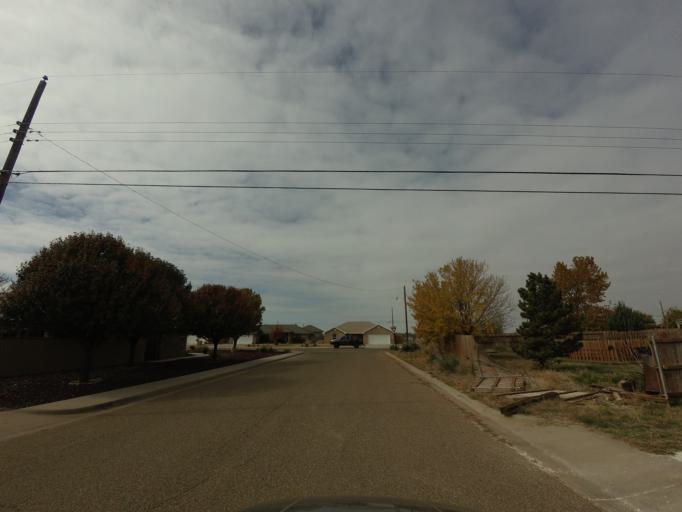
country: US
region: New Mexico
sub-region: Curry County
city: Clovis
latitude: 34.4315
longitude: -103.2262
